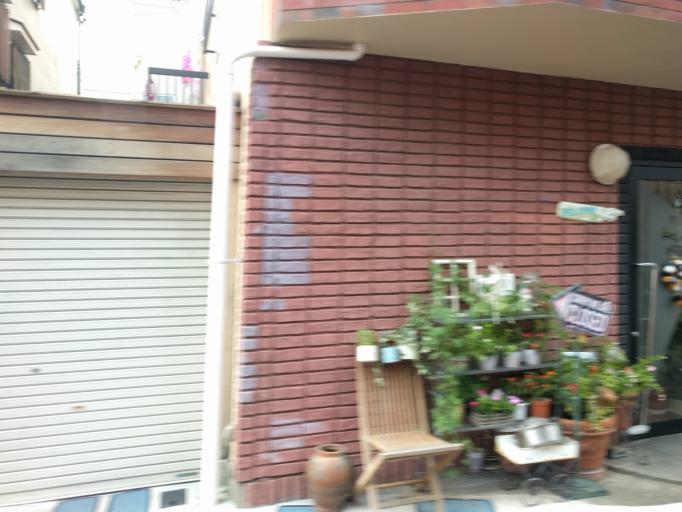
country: JP
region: Tokyo
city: Tokyo
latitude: 35.6801
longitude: 139.6730
